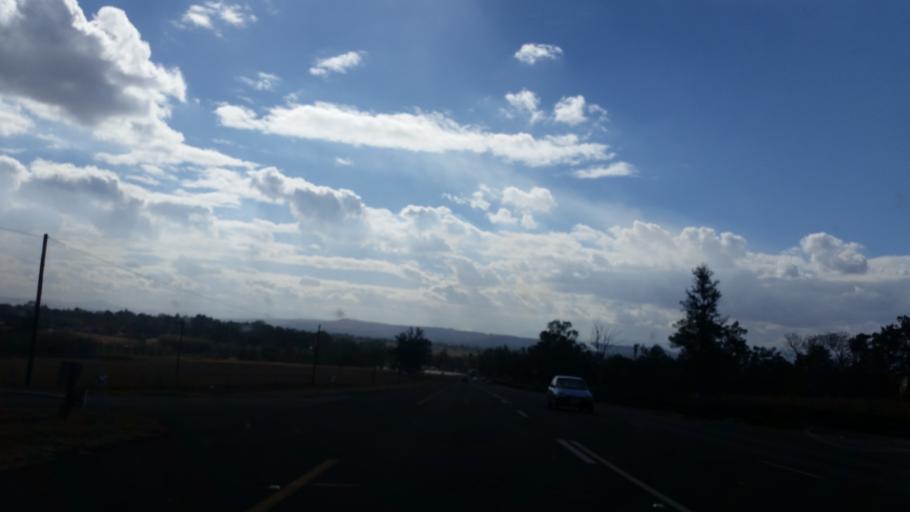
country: ZA
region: KwaZulu-Natal
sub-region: Amajuba District Municipality
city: Newcastle
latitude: -27.7984
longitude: 29.9562
